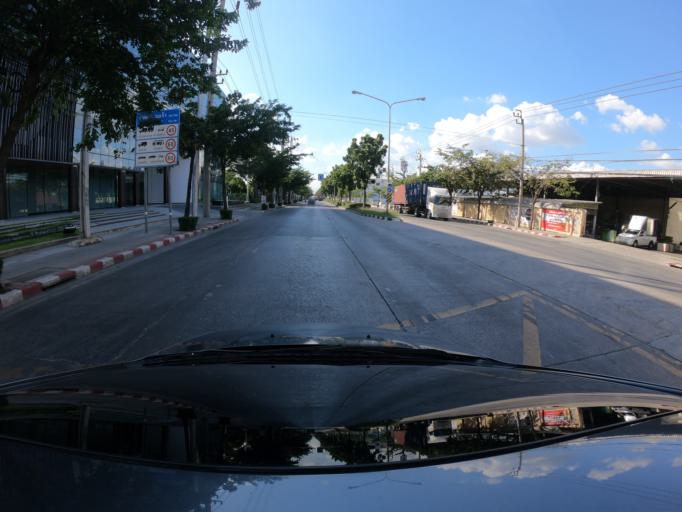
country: TH
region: Bangkok
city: Phra Khanong
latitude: 13.6751
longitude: 100.5960
